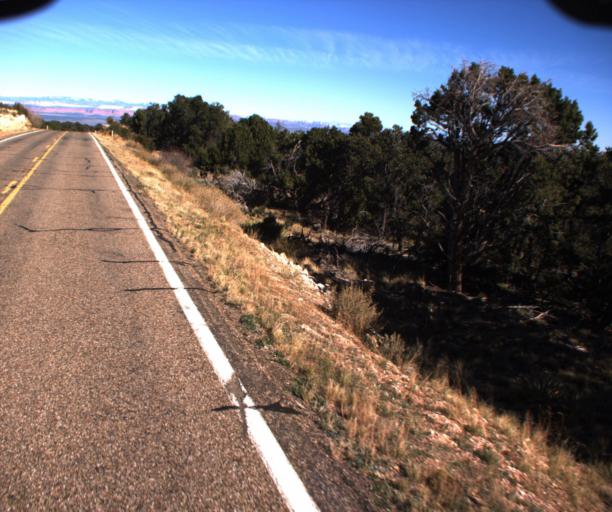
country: US
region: Arizona
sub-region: Coconino County
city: Fredonia
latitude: 36.8230
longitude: -112.2539
